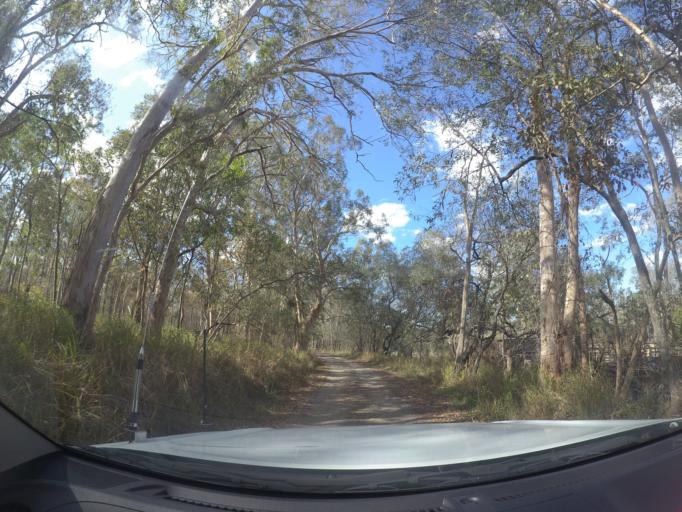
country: AU
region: Queensland
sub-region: Logan
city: North Maclean
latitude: -27.7897
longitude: 152.9885
